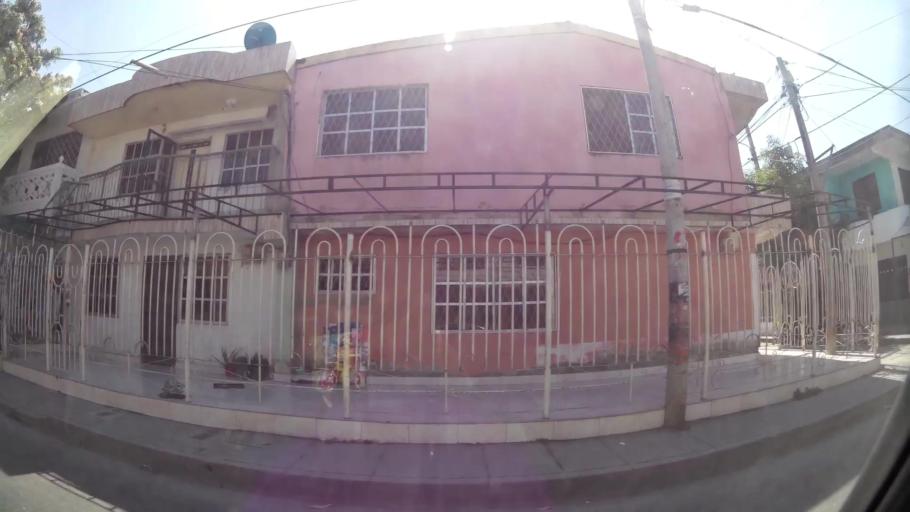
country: CO
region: Bolivar
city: Cartagena
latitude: 10.3858
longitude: -75.4572
